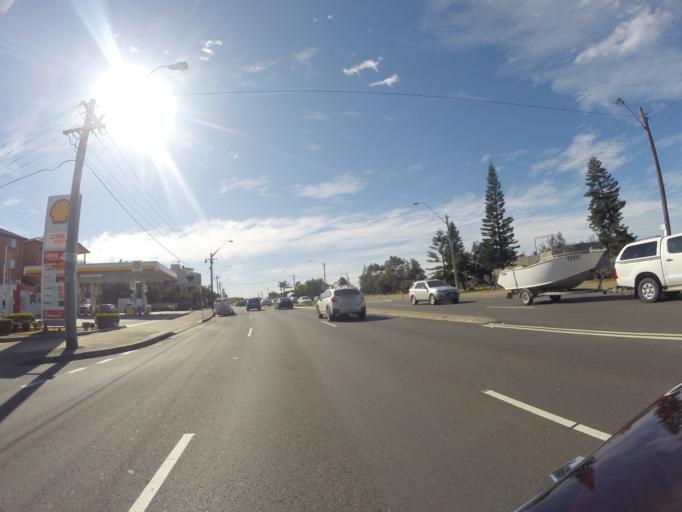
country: AU
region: New South Wales
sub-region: Rockdale
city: Brighton-Le-Sands
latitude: -33.9582
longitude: 151.1577
